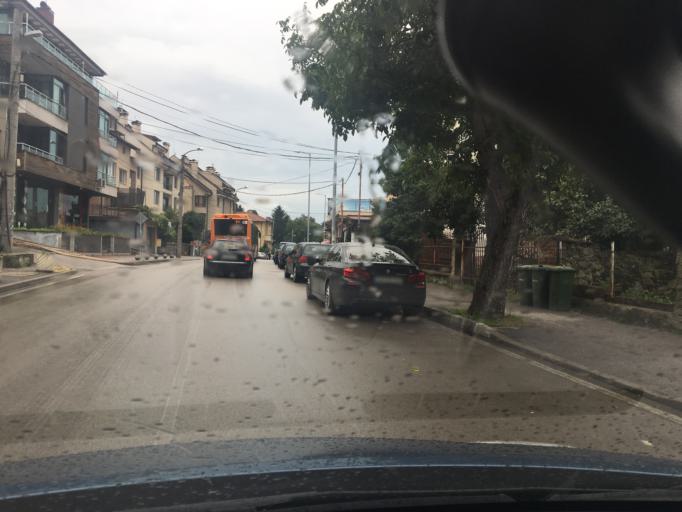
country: BG
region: Sofia-Capital
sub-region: Stolichna Obshtina
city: Sofia
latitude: 42.6293
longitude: 23.3085
